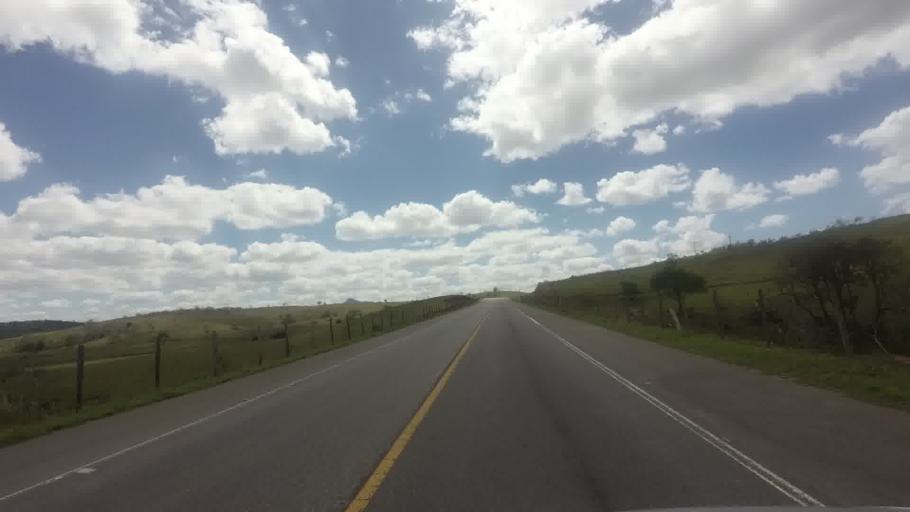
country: BR
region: Minas Gerais
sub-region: Recreio
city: Recreio
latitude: -21.6812
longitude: -42.3980
